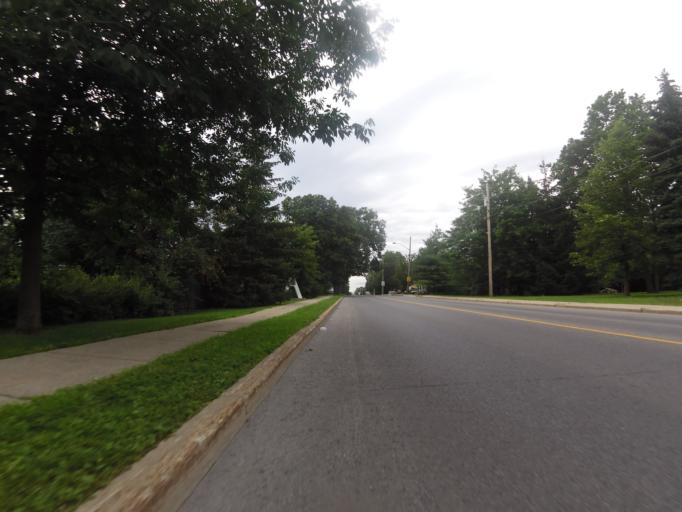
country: CA
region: Ontario
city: Carleton Place
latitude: 45.1315
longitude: -76.1310
